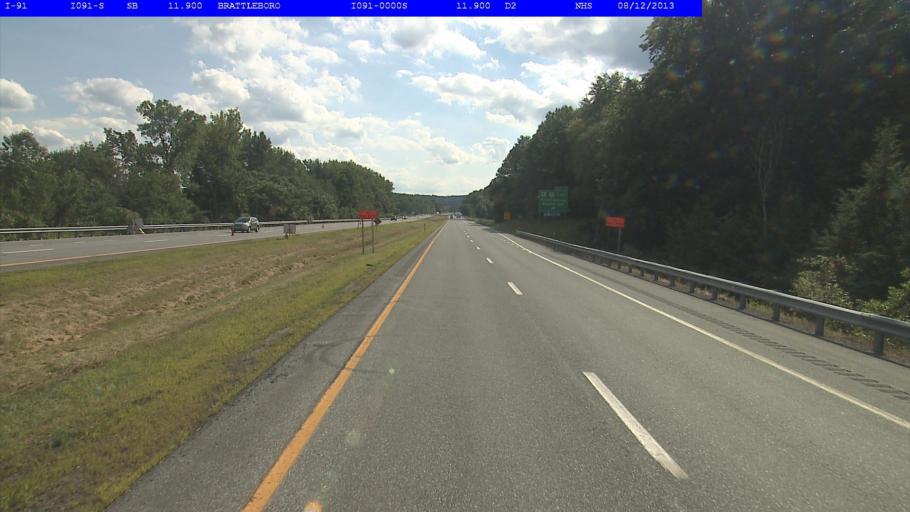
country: US
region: Vermont
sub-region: Windham County
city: Brattleboro
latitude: 42.8903
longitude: -72.5555
